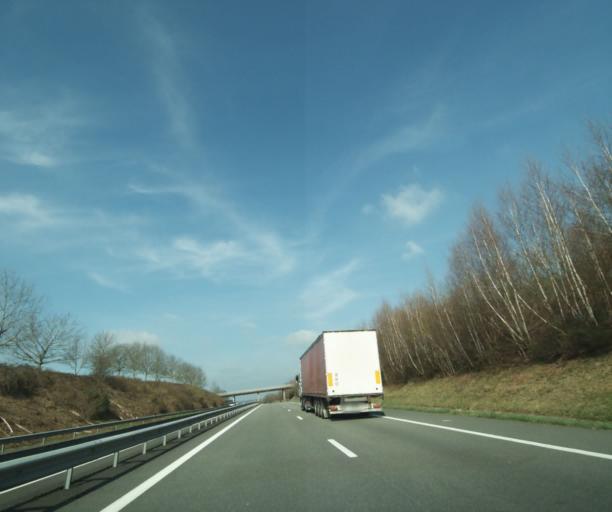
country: FR
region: Limousin
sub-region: Departement de la Haute-Vienne
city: Saint-Sulpice-les-Feuilles
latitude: 46.3264
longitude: 1.4181
